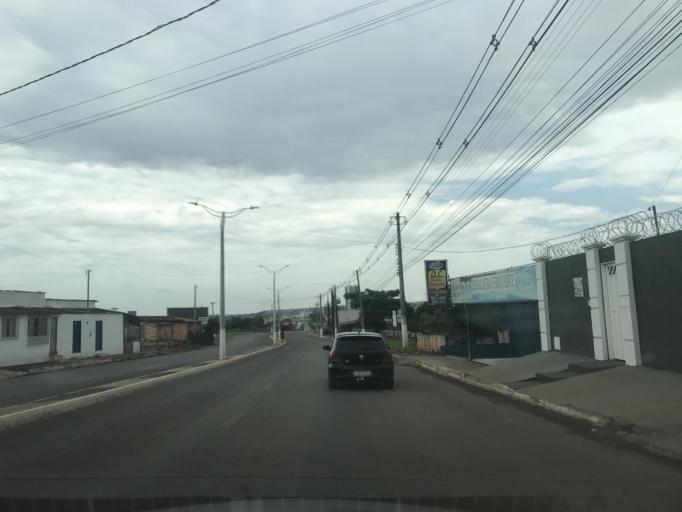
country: BR
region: Goias
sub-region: Luziania
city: Luziania
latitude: -16.2422
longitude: -47.9449
